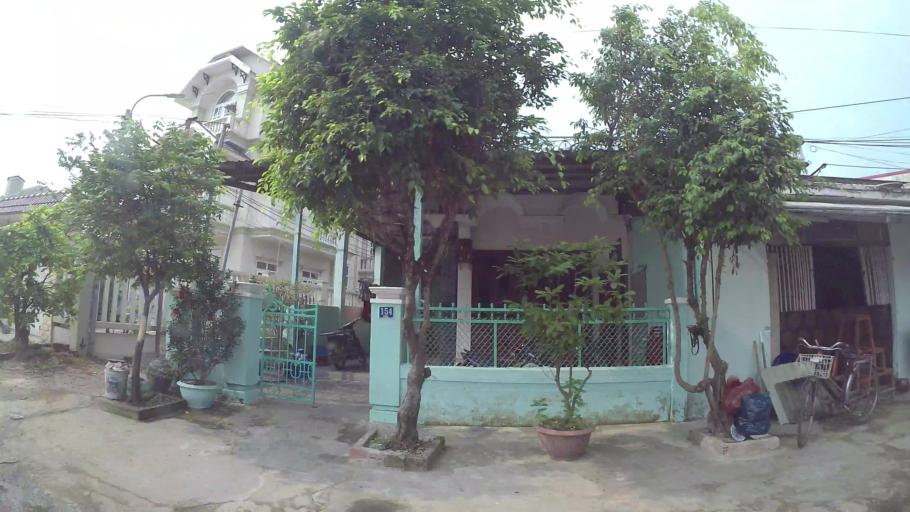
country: VN
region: Da Nang
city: Son Tra
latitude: 16.0887
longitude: 108.2481
